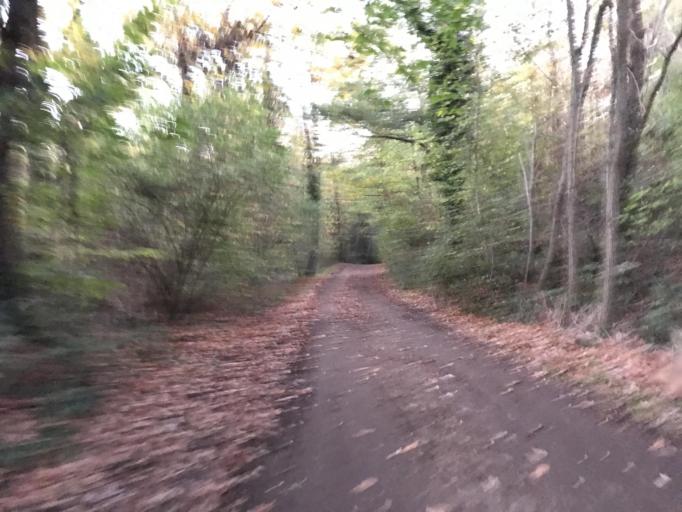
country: FR
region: Ile-de-France
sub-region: Departement de l'Essonne
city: Villejust
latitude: 48.6759
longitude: 2.2512
